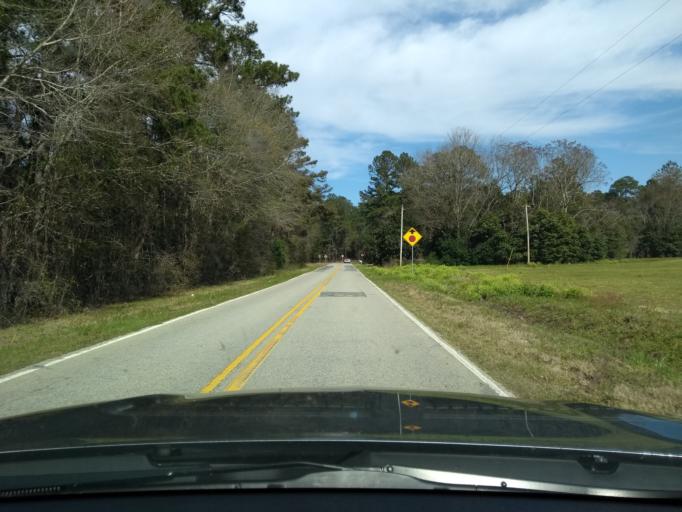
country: US
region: Georgia
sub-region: Bulloch County
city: Brooklet
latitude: 32.4858
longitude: -81.6233
